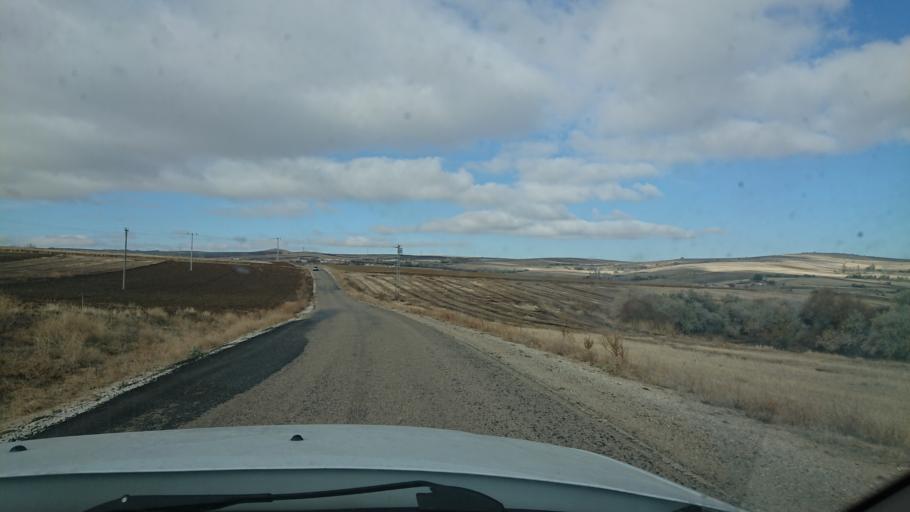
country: TR
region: Aksaray
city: Agacoren
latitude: 38.8194
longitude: 33.9768
